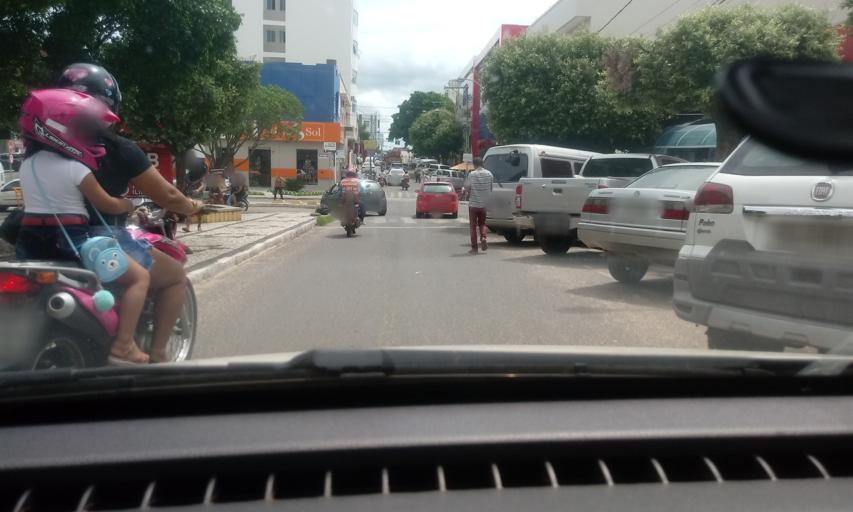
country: BR
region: Bahia
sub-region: Guanambi
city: Guanambi
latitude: -14.2270
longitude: -42.7794
